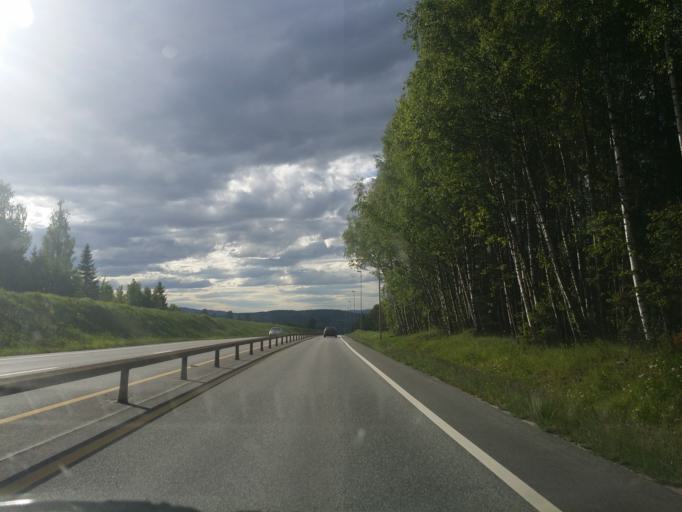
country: NO
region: Hedmark
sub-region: Stange
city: Stange
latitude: 60.7726
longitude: 11.1599
